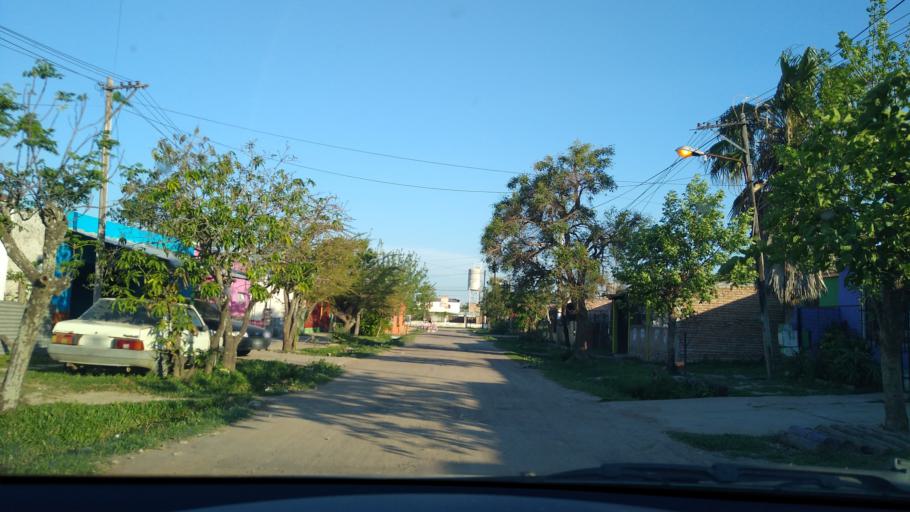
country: AR
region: Chaco
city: Puerto Vilelas
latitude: -27.5124
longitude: -58.9453
